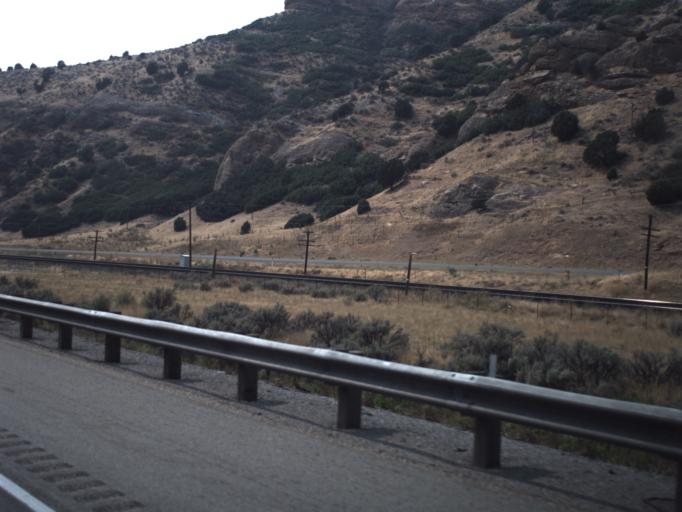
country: US
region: Utah
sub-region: Summit County
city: Coalville
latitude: 41.0182
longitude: -111.3664
